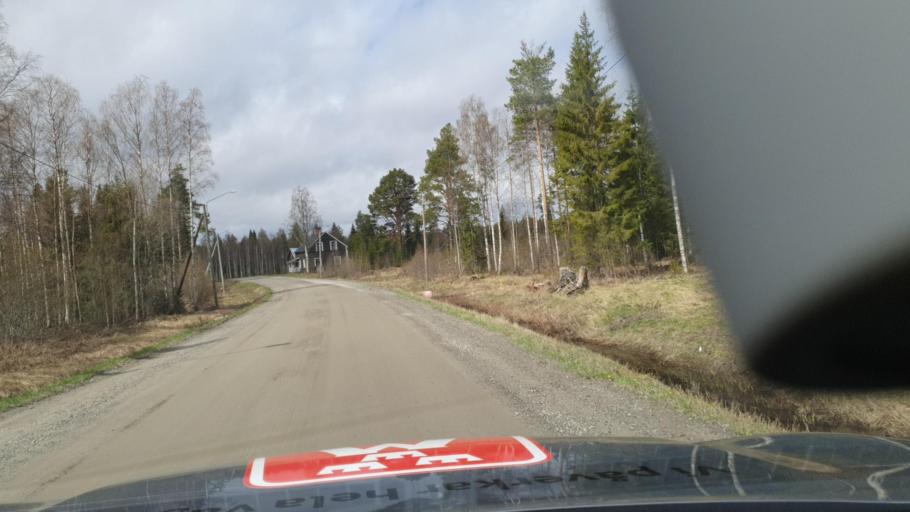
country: SE
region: Vaesterbotten
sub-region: Bjurholms Kommun
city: Bjurholm
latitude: 63.6975
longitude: 18.9502
